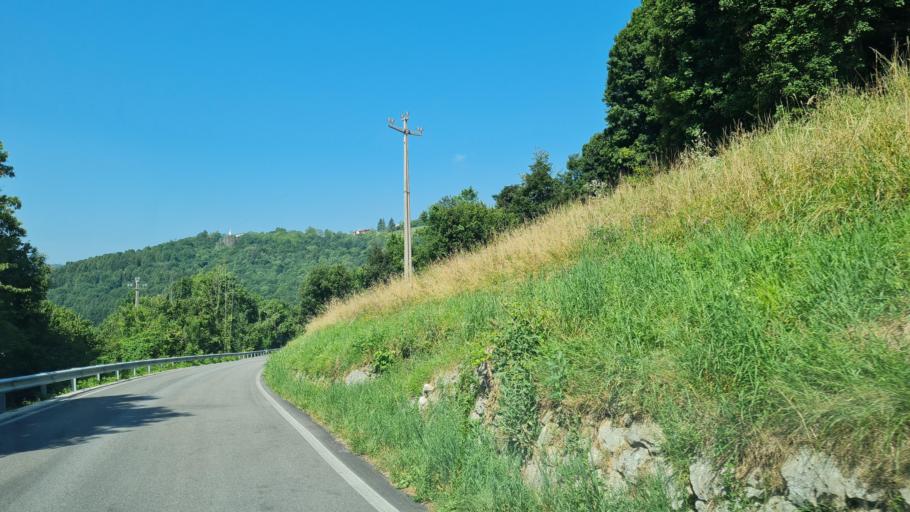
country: IT
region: Veneto
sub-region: Provincia di Vicenza
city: Conco
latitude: 45.7905
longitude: 11.6162
